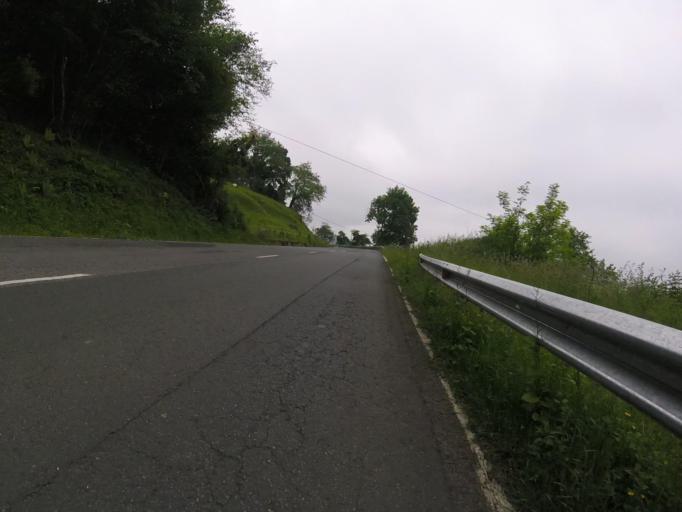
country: ES
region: Navarre
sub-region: Provincia de Navarra
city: Zugarramurdi
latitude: 43.2702
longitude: -1.4945
